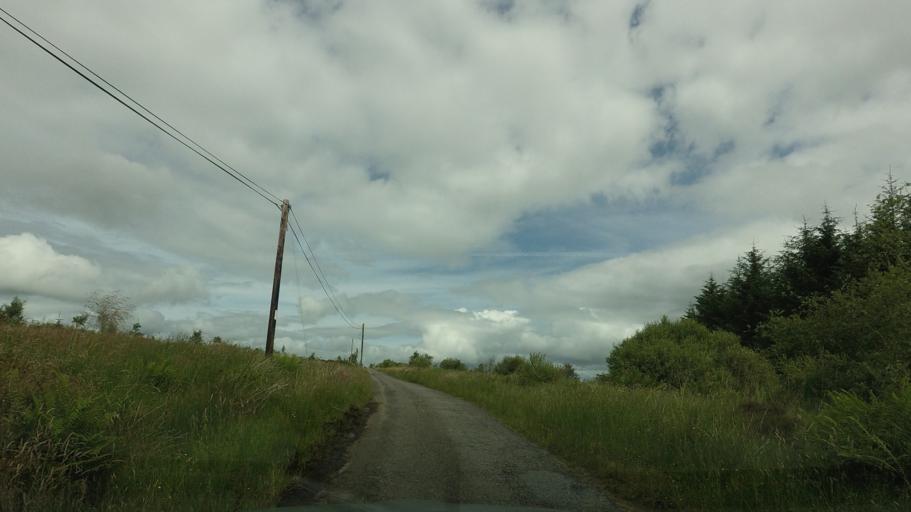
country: GB
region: Scotland
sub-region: Stirling
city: Killearn
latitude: 56.0872
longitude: -4.4368
